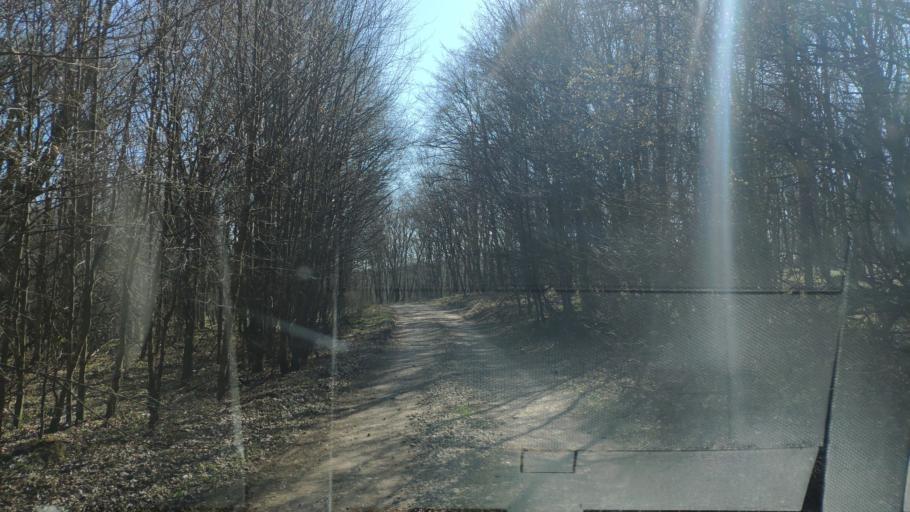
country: SK
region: Kosicky
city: Roznava
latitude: 48.6011
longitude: 20.4111
